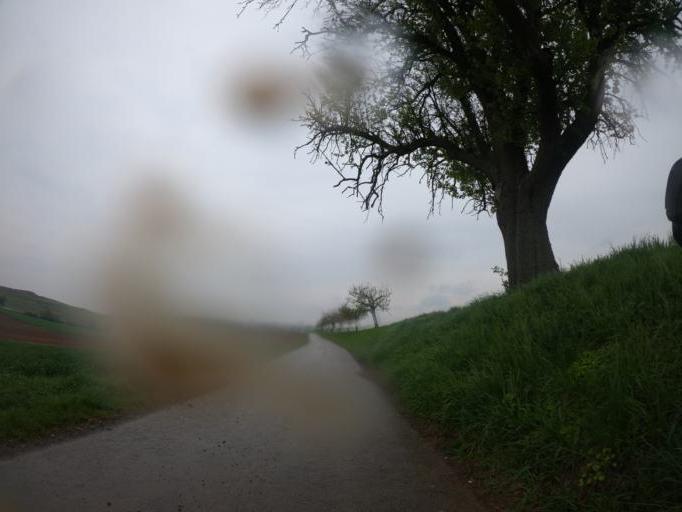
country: DE
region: Baden-Wuerttemberg
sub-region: Regierungsbezirk Stuttgart
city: Hemmingen
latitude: 48.8822
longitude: 9.0497
